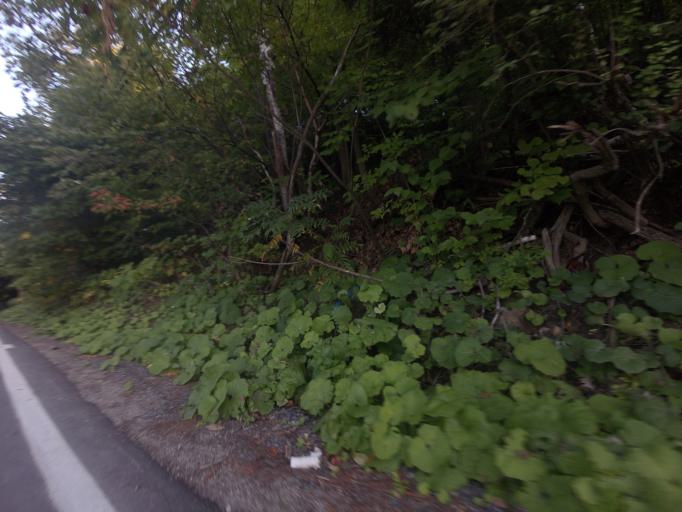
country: CA
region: Quebec
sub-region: Monteregie
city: Hudson
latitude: 45.4684
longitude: -74.1644
